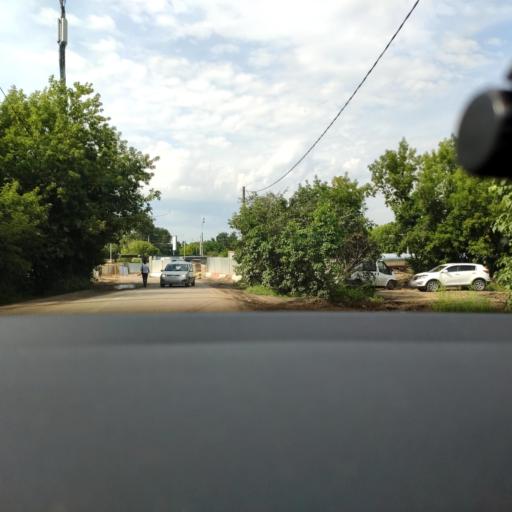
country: RU
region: Moskovskaya
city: Fili
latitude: 55.7497
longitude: 37.4514
